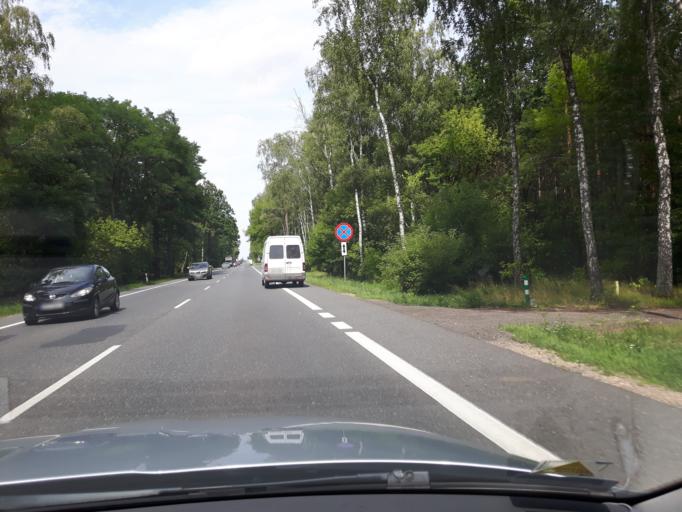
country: PL
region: Masovian Voivodeship
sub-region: Powiat mlawski
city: Strzegowo
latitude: 52.9134
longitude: 20.2865
